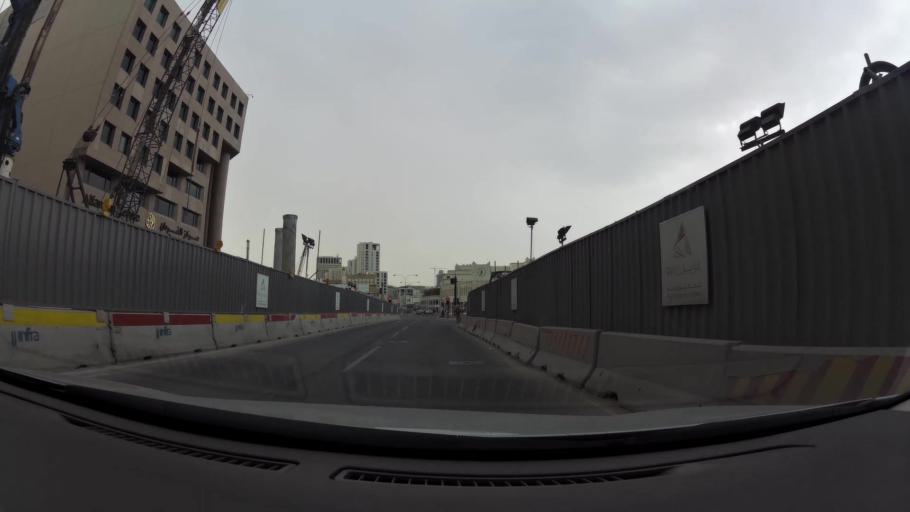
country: QA
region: Baladiyat ad Dawhah
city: Doha
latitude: 25.2862
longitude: 51.5358
